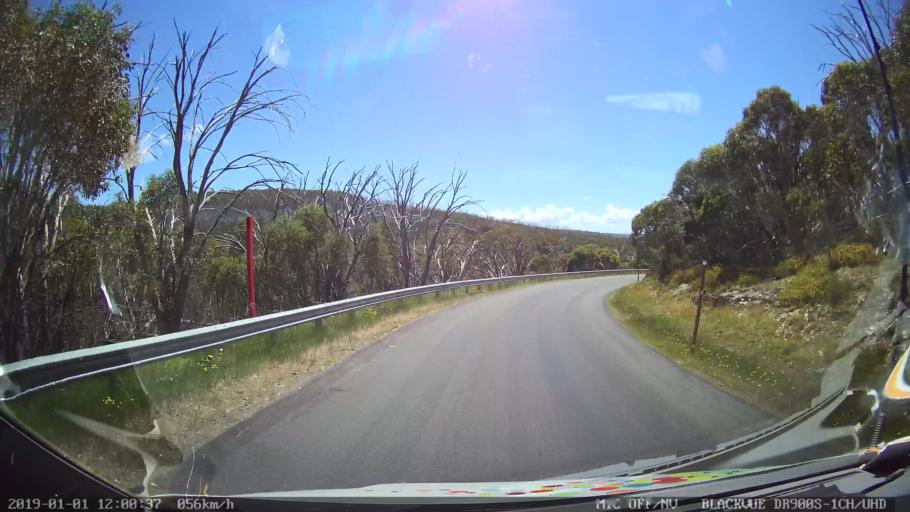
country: AU
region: New South Wales
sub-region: Snowy River
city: Jindabyne
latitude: -35.8834
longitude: 148.4600
